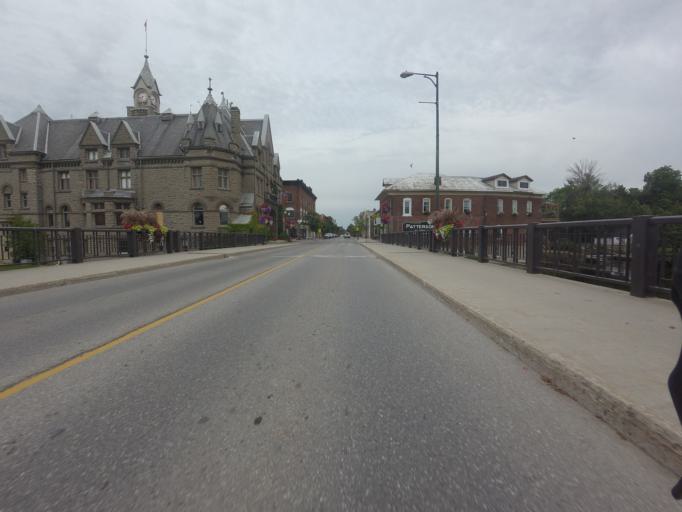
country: CA
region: Ontario
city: Carleton Place
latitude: 45.1407
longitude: -76.1471
